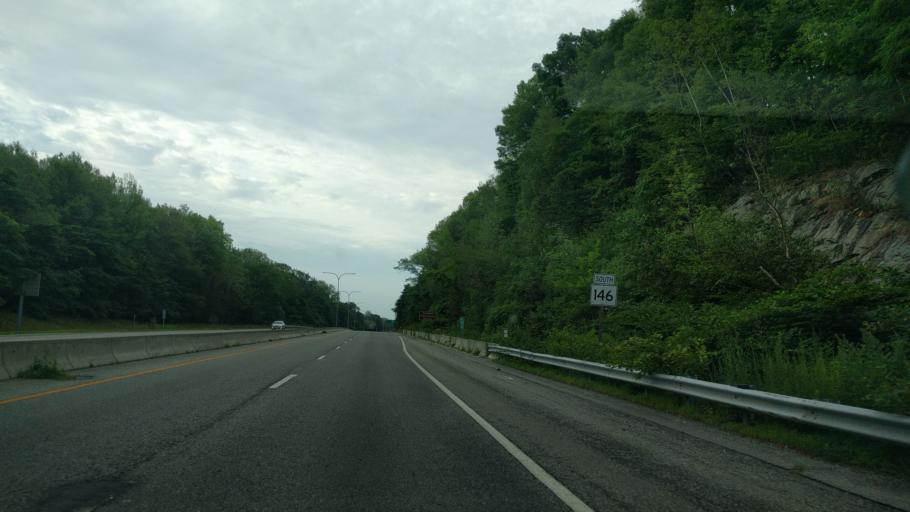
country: US
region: Rhode Island
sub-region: Providence County
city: Valley Falls
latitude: 41.9083
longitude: -71.4503
